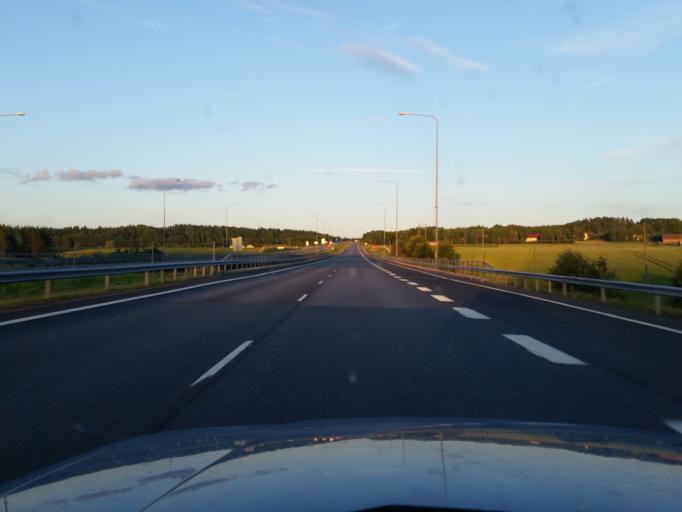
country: FI
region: Varsinais-Suomi
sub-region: Salo
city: Salo
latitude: 60.4157
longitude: 23.1748
